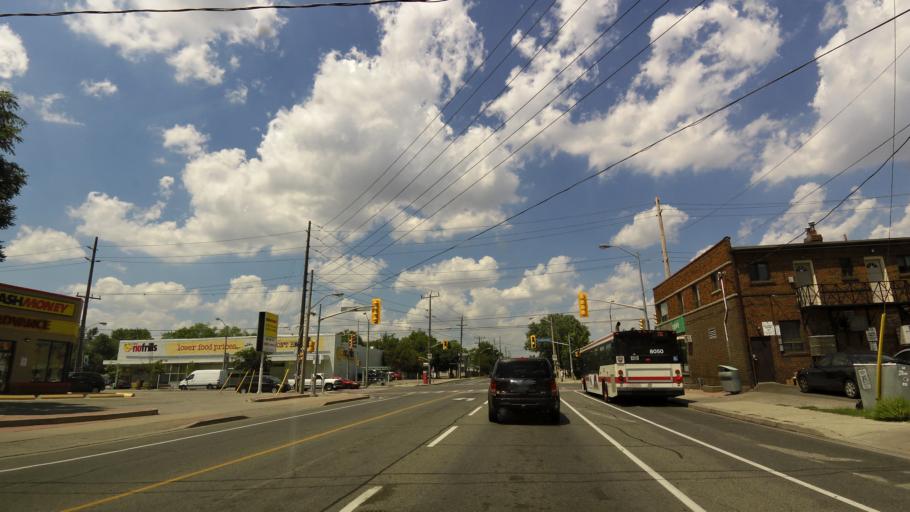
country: CA
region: Ontario
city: Etobicoke
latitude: 43.6259
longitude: -79.5024
